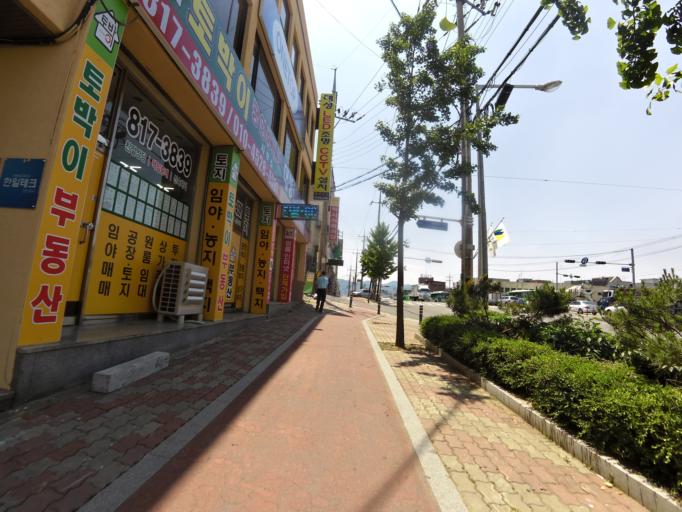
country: KR
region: Gyeongsangbuk-do
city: Gyeongsan-si
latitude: 35.8399
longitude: 128.7587
